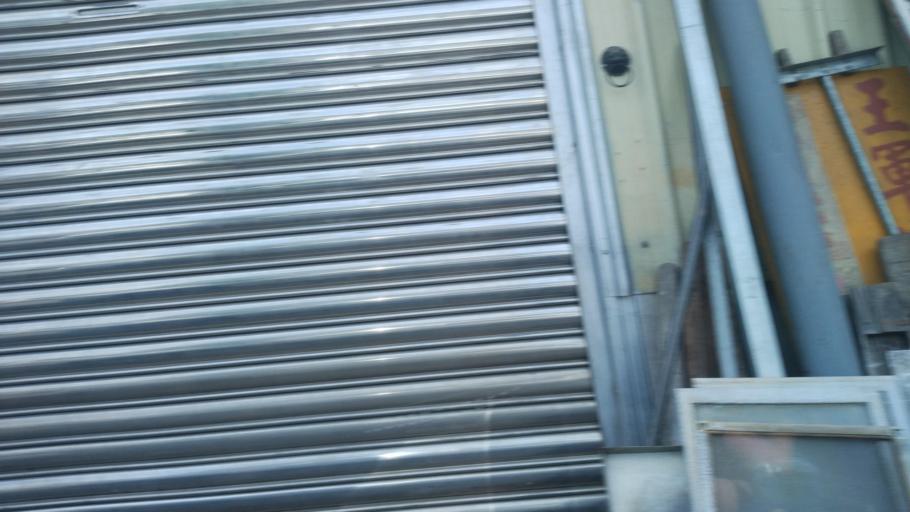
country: TW
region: Taipei
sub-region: Taipei
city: Banqiao
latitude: 24.9479
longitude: 121.4922
